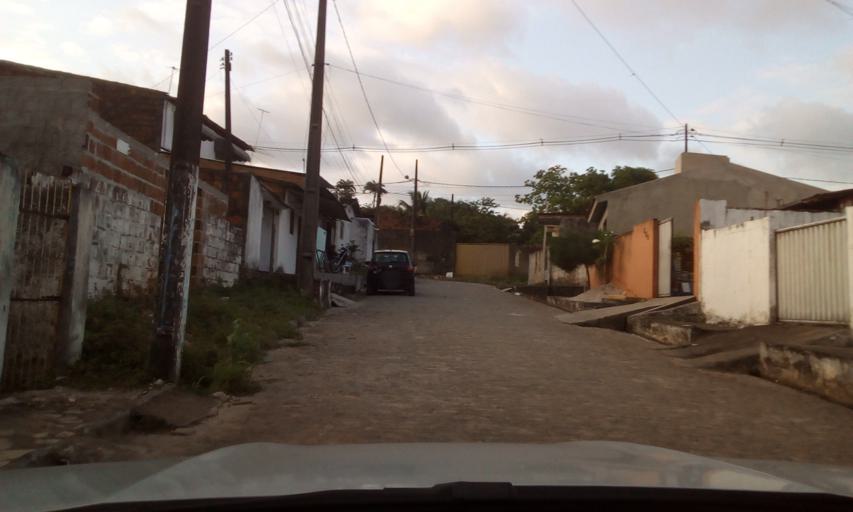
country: BR
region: Paraiba
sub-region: Bayeux
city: Bayeux
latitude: -7.1826
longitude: -34.8921
